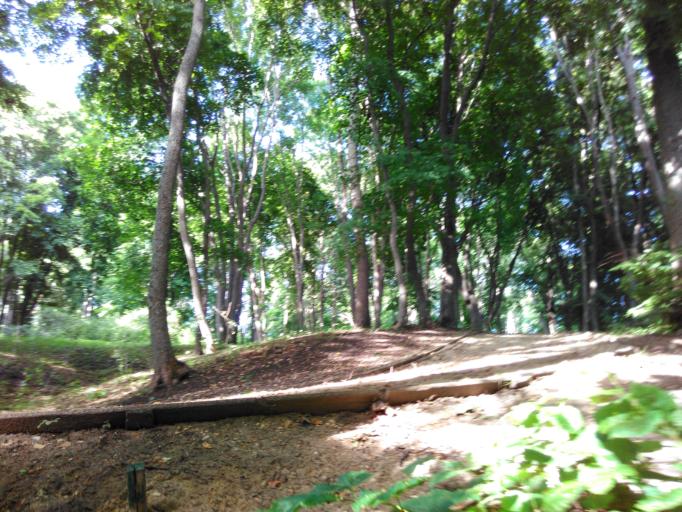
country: RU
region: Penza
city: Lermontovo
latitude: 52.9615
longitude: 43.6705
